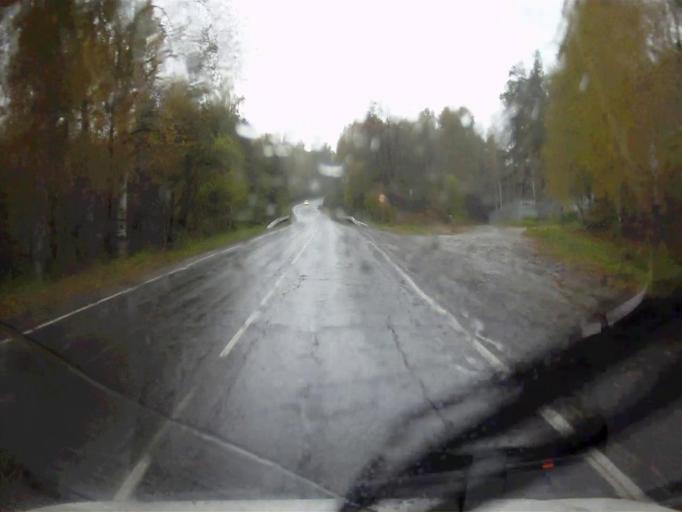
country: RU
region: Chelyabinsk
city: Kyshtym
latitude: 55.9101
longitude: 60.4352
